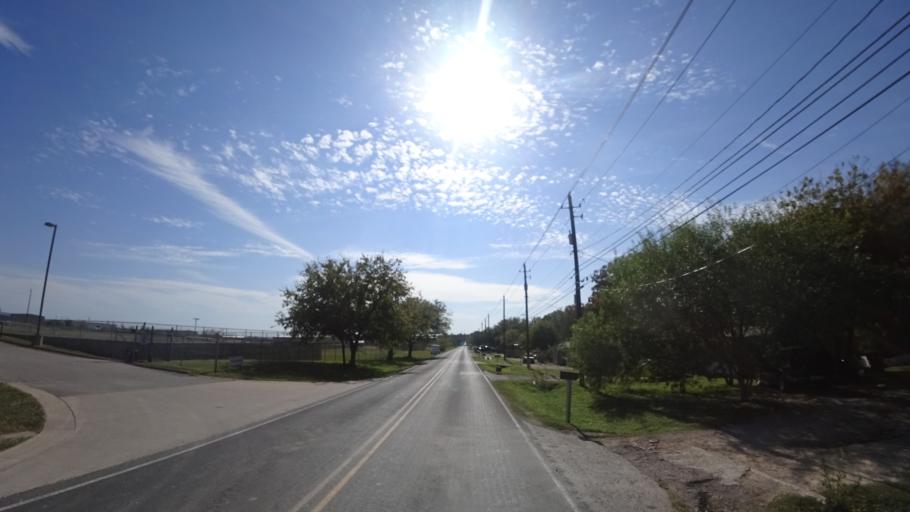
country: US
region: Texas
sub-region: Travis County
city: Pflugerville
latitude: 30.4059
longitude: -97.6326
